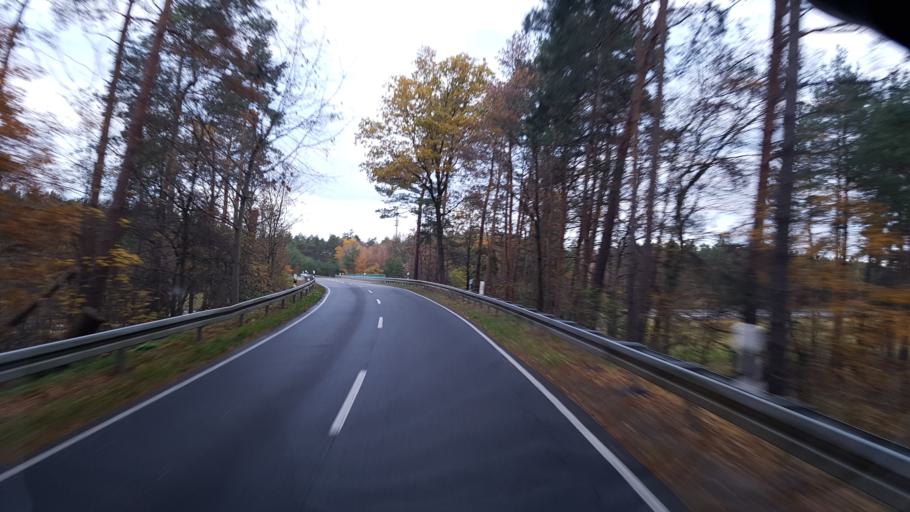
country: DE
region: Brandenburg
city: Ortrand
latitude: 51.3950
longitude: 13.7664
